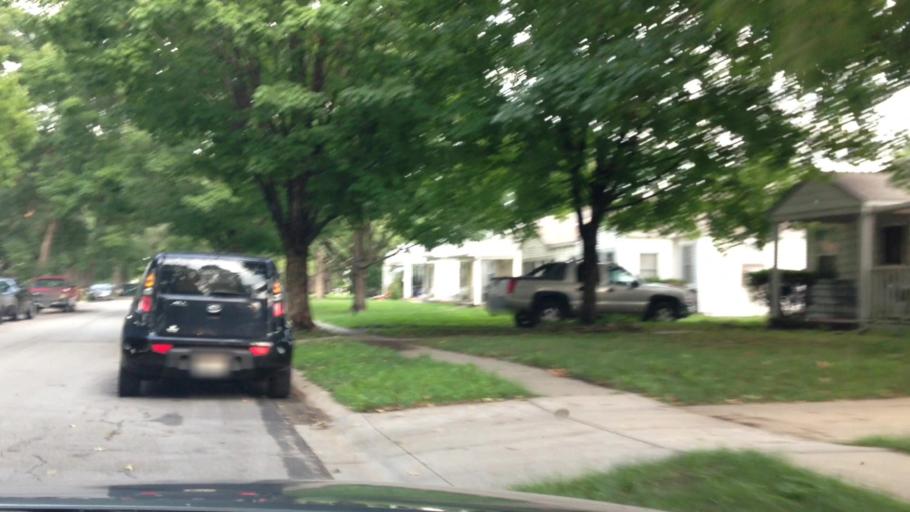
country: US
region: Missouri
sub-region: Clay County
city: North Kansas City
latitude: 39.1484
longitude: -94.5757
